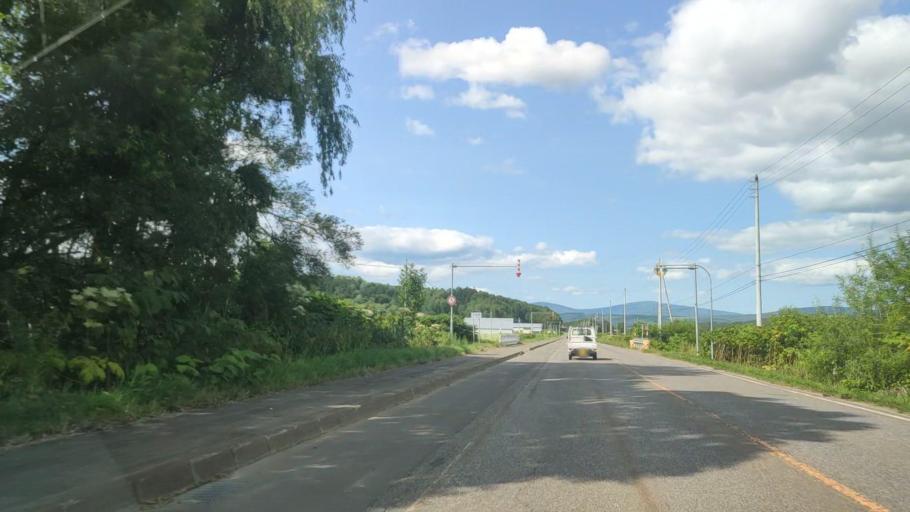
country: JP
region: Hokkaido
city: Nayoro
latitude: 44.3983
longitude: 142.3951
